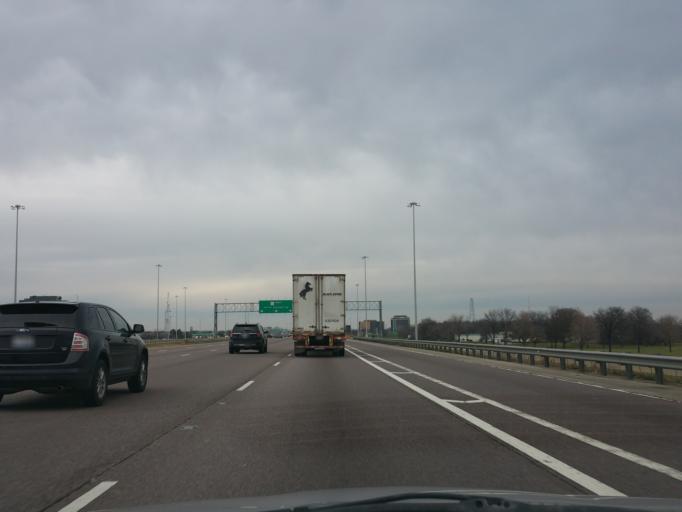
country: US
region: Illinois
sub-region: Cook County
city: Rolling Meadows
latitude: 42.0439
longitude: -88.0300
